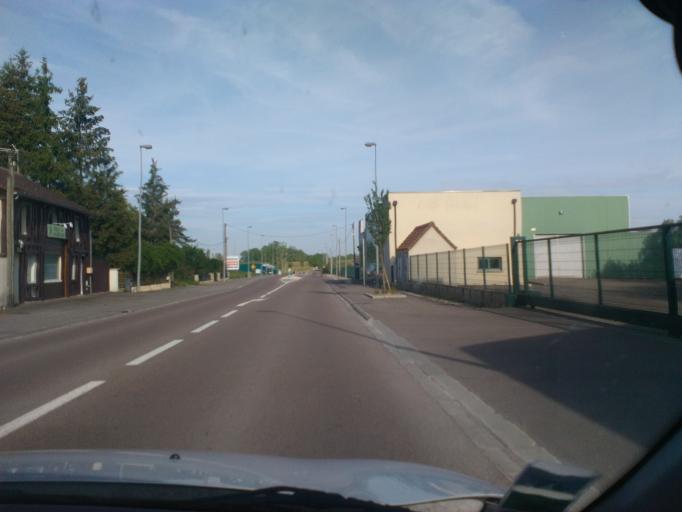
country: FR
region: Champagne-Ardenne
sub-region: Departement de l'Aube
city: Vendeuvre-sur-Barse
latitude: 48.2365
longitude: 4.4545
